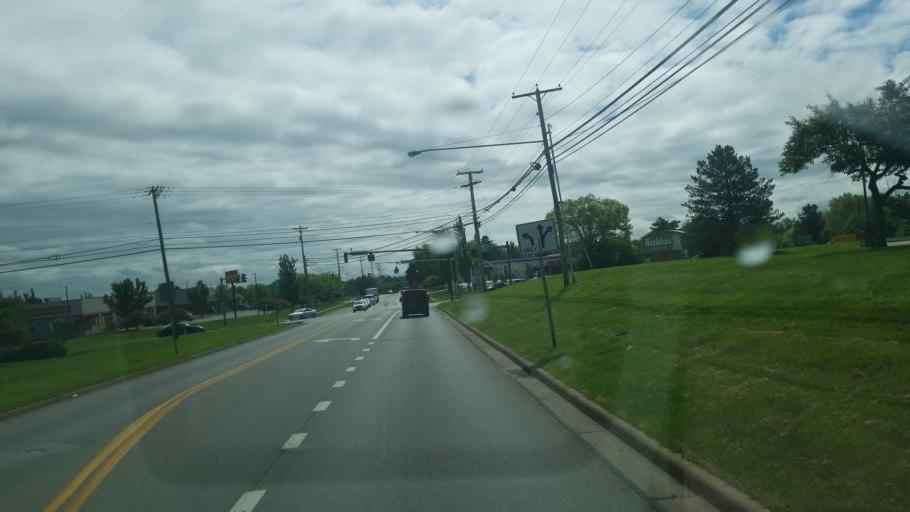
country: US
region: Ohio
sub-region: Wayne County
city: Wooster
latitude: 40.8432
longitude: -81.9435
